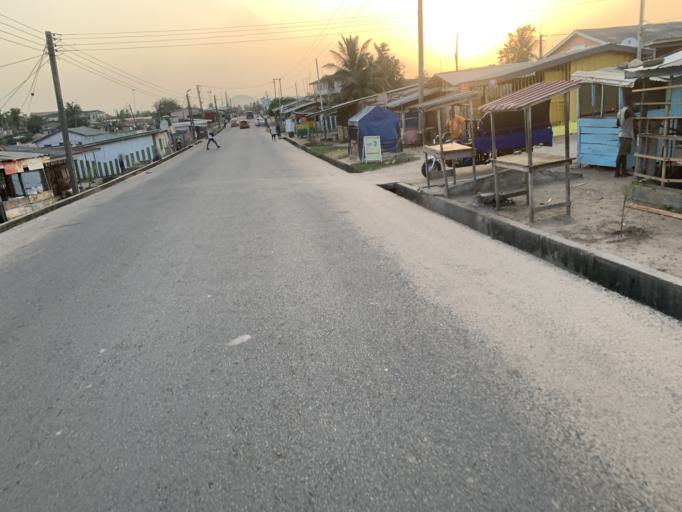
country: GH
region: Central
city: Winneba
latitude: 5.3517
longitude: -0.6204
